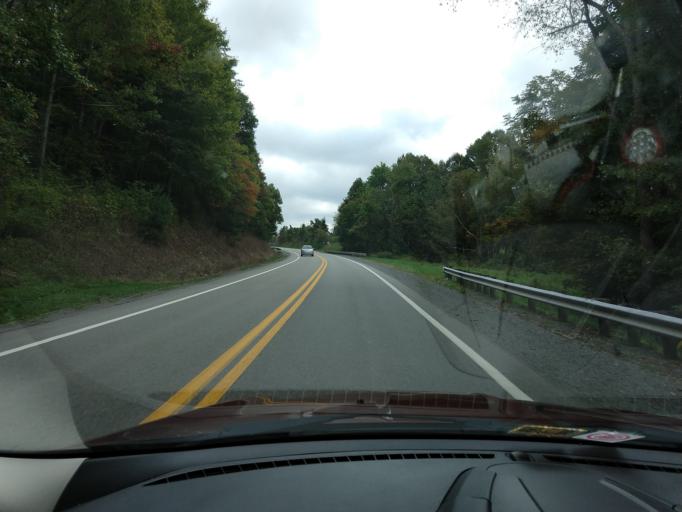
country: US
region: West Virginia
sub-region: Barbour County
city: Belington
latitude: 39.0901
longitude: -79.9847
